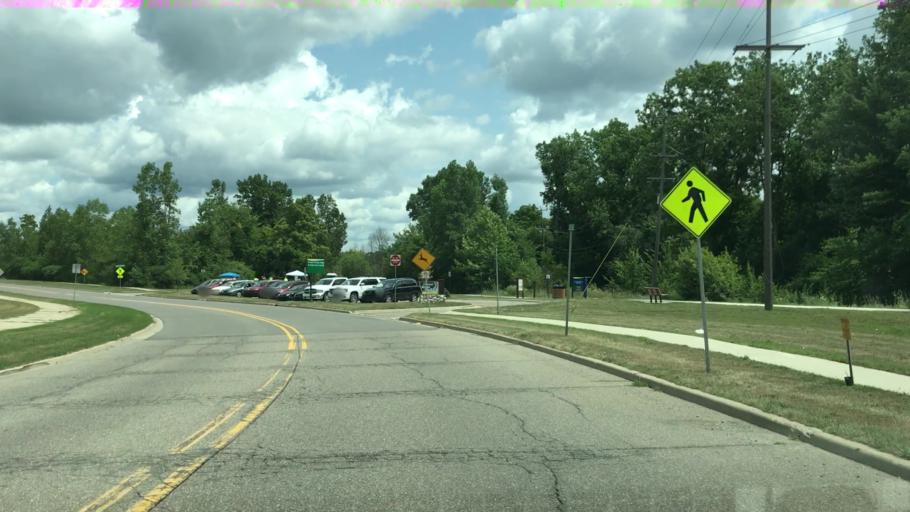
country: US
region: Michigan
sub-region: Oakland County
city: Rochester
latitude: 42.6797
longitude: -83.1236
